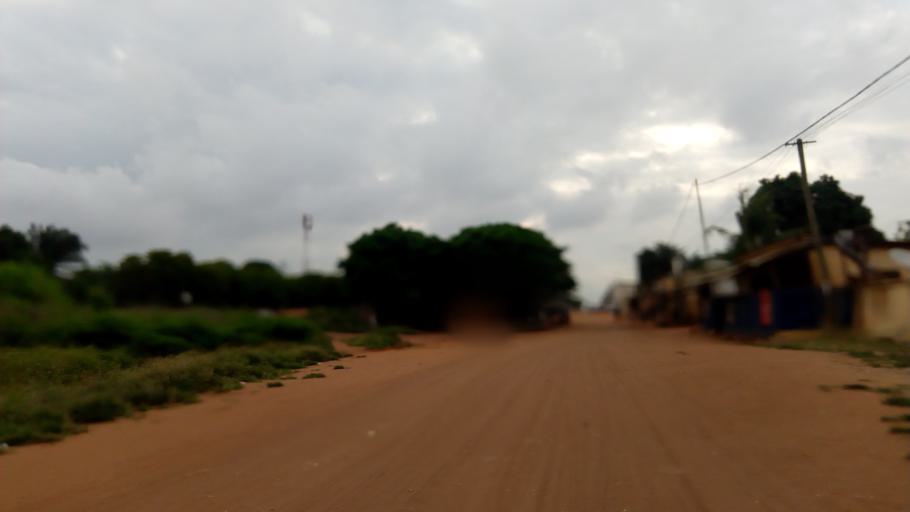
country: TG
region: Maritime
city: Lome
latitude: 6.1750
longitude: 1.1928
